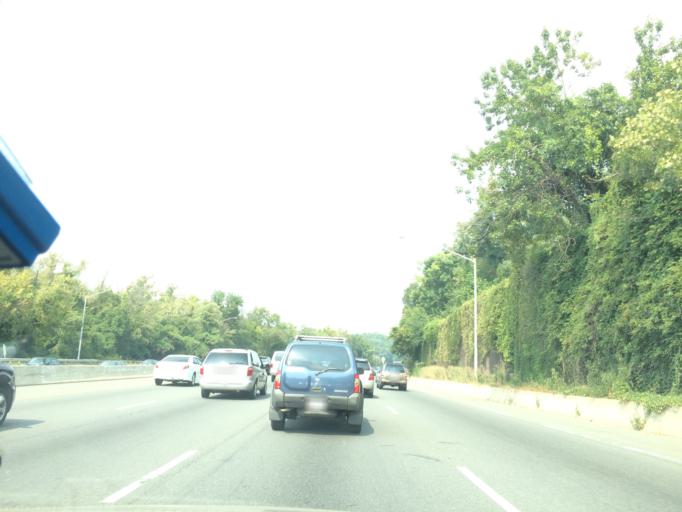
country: US
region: Maryland
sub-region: Montgomery County
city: Forest Glen
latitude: 39.0080
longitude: -77.0671
